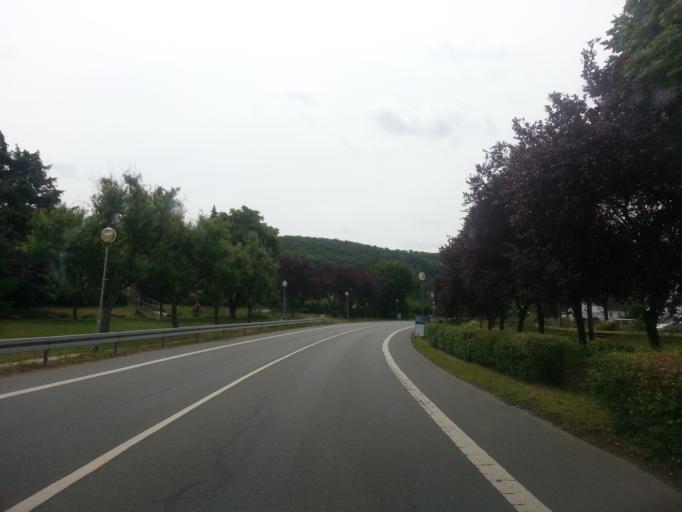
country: DE
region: Hesse
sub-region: Regierungsbezirk Darmstadt
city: Seeheim-Jugenheim
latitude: 49.7655
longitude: 8.6455
